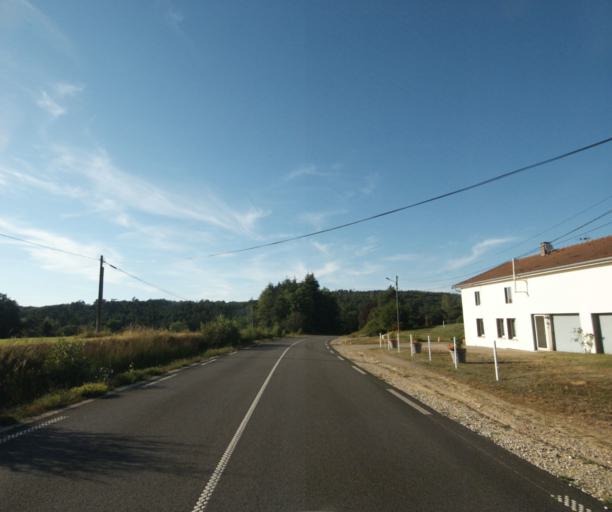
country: FR
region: Lorraine
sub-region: Departement des Vosges
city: Urimenil
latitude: 48.1260
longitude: 6.4299
